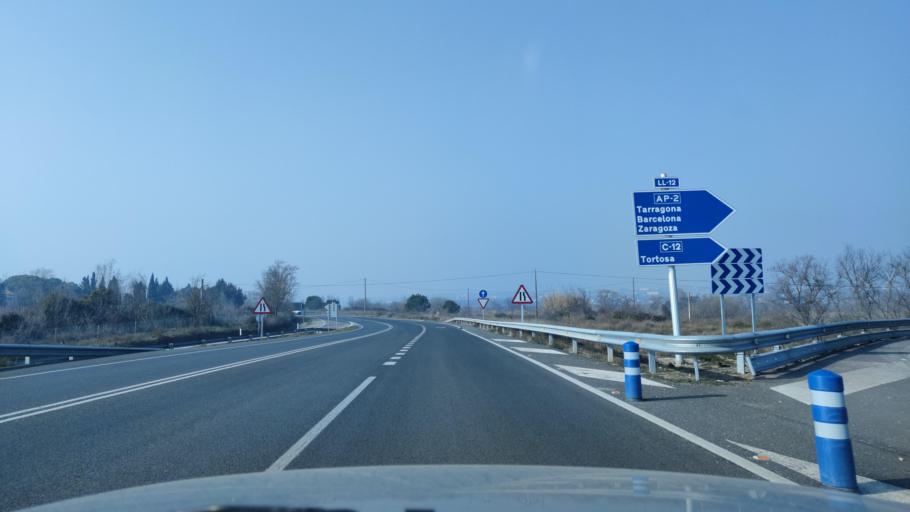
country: ES
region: Catalonia
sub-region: Provincia de Lleida
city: Lleida
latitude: 41.5816
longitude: 0.6225
